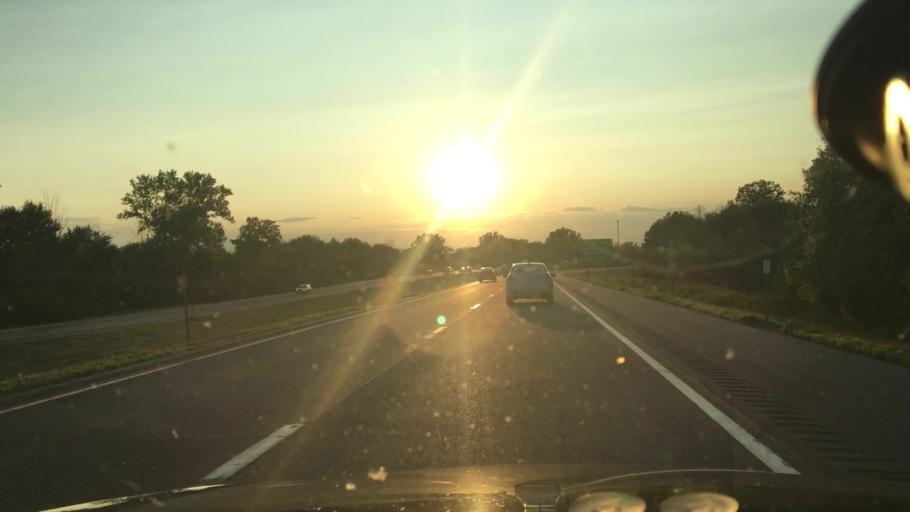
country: US
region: New York
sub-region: Erie County
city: Blasdell
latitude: 42.8095
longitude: -78.7866
